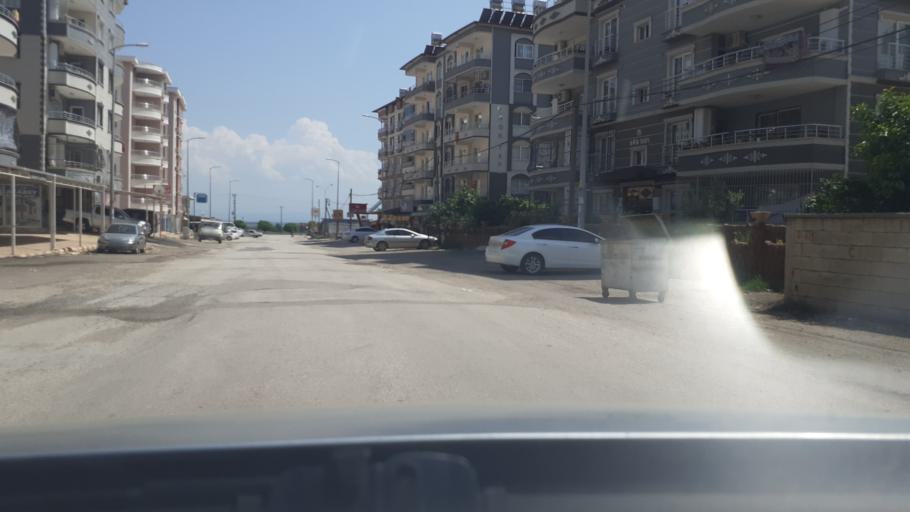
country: TR
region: Hatay
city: Kirikhan
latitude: 36.4814
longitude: 36.3554
